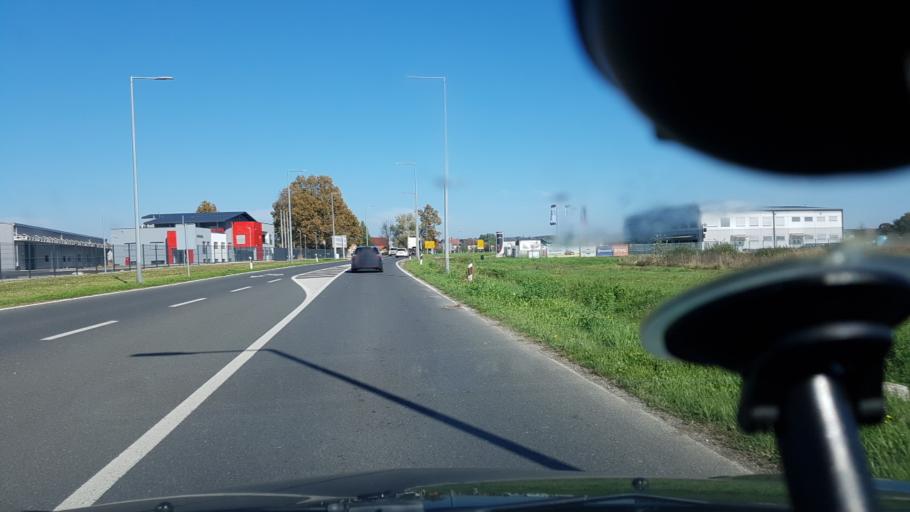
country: HR
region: Zagrebacka
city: Lupoglav
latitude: 45.7076
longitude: 16.4103
